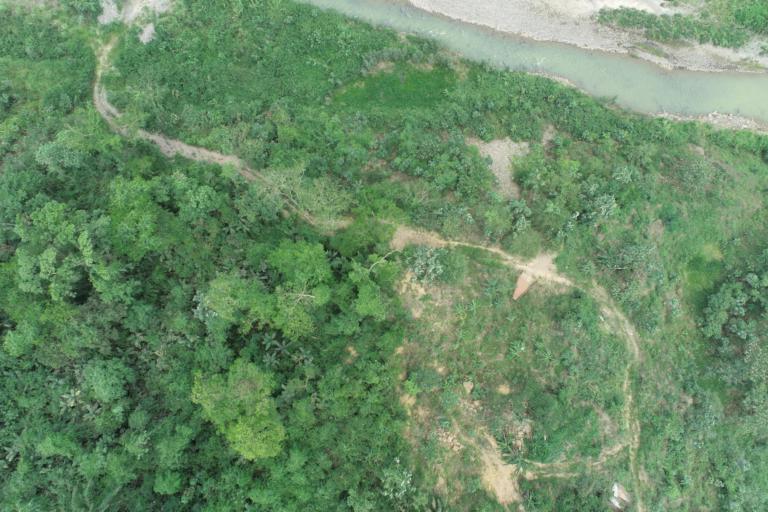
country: BO
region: La Paz
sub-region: Provincia Larecaja
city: Guanay
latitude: -15.7667
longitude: -67.6643
